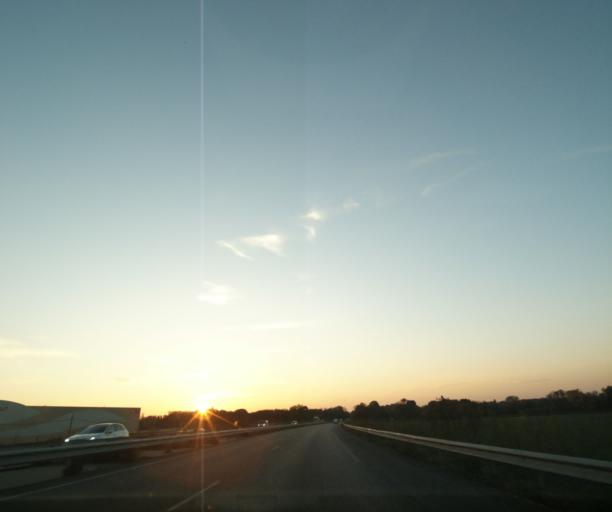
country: FR
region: Provence-Alpes-Cote d'Azur
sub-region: Departement des Bouches-du-Rhone
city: Saint-Martin-de-Crau
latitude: 43.6295
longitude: 4.7606
